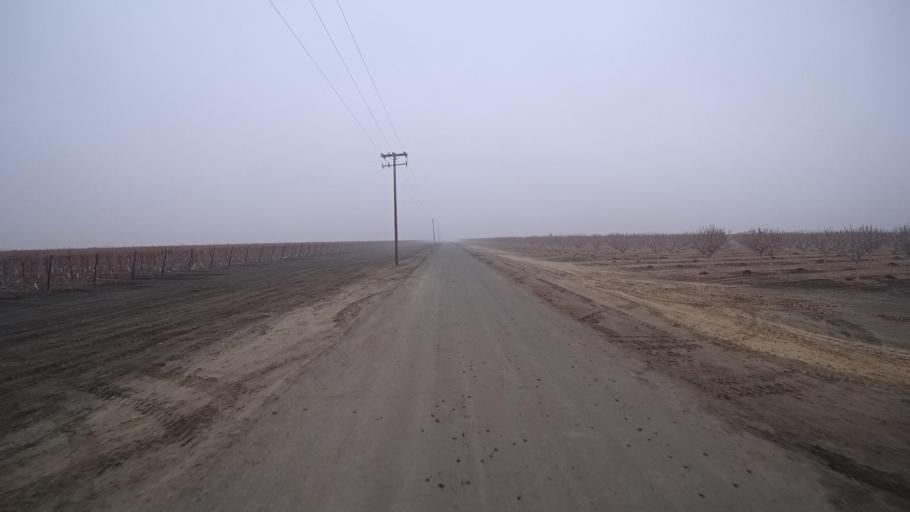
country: US
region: California
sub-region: Kern County
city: Buttonwillow
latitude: 35.4269
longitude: -119.5204
